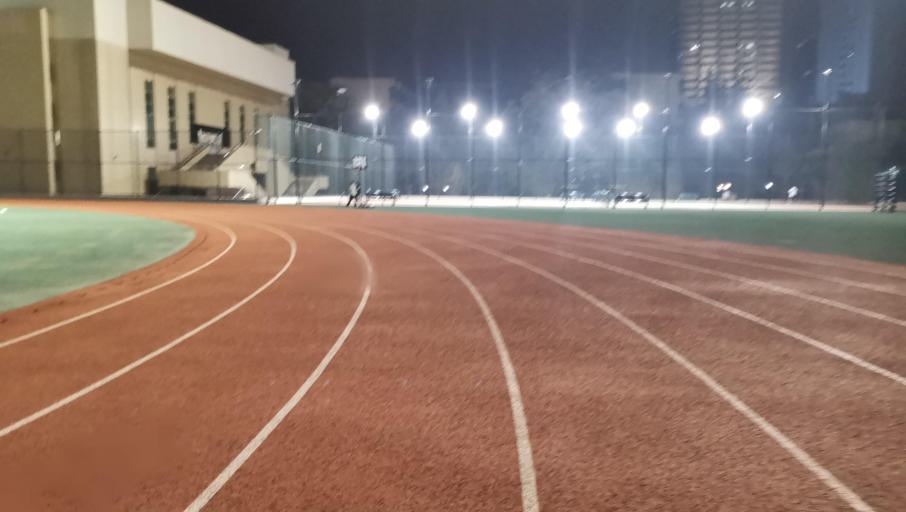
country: CN
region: Shandong Sheng
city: Jinan
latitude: 36.6497
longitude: 117.0128
